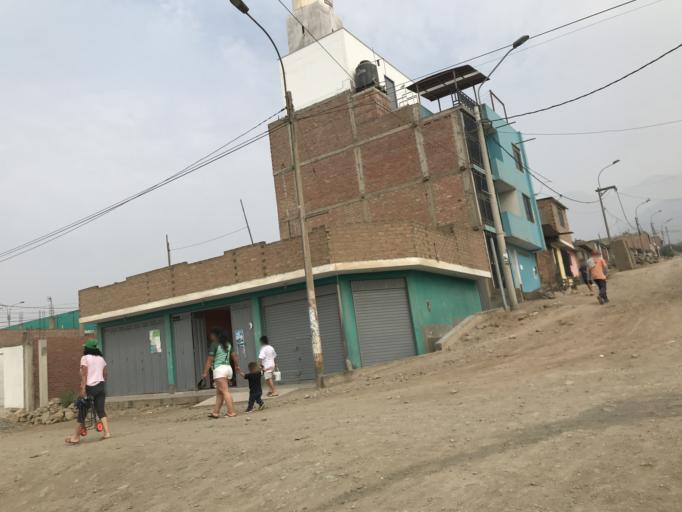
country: PE
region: Lima
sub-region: Lima
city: Carabayllo
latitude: -11.8178
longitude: -77.0452
